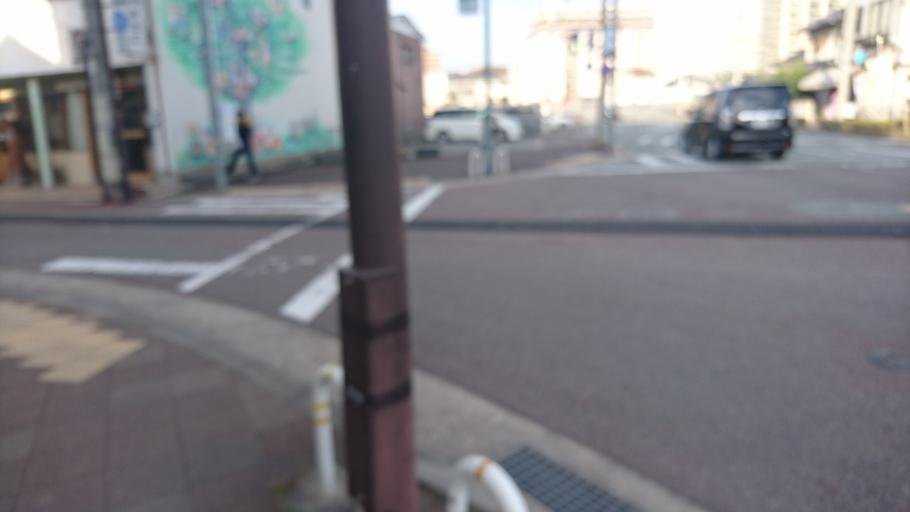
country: JP
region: Hyogo
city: Sandacho
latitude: 34.8850
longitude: 135.2256
